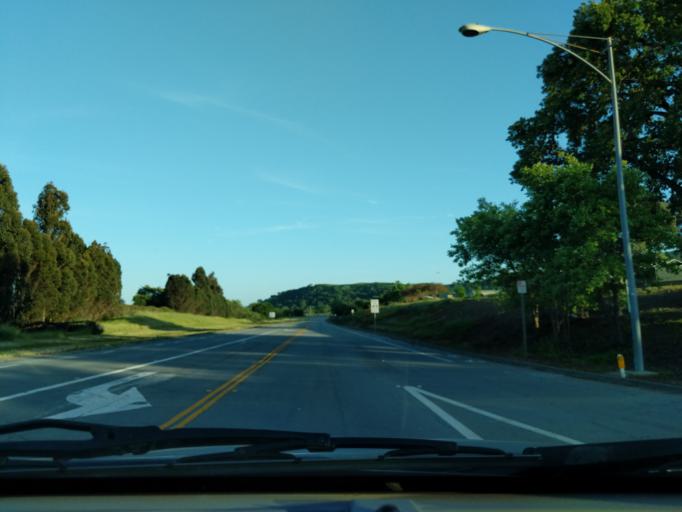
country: US
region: California
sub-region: Santa Clara County
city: Gilroy
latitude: 36.9762
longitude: -121.5681
